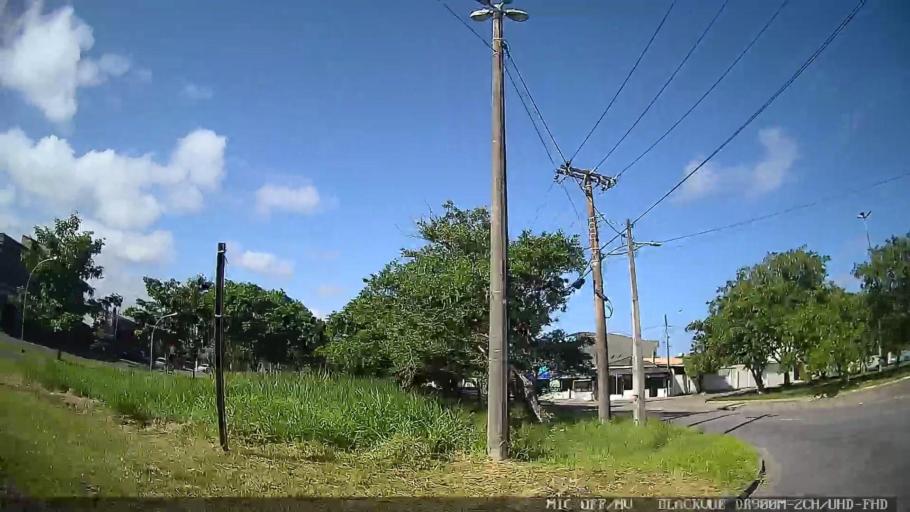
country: BR
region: Sao Paulo
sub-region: Peruibe
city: Peruibe
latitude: -24.3071
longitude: -46.9949
